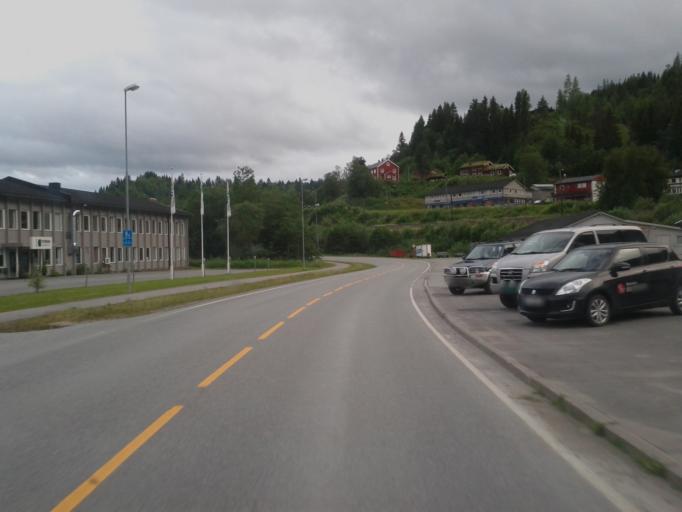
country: NO
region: Sor-Trondelag
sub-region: Midtre Gauldal
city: Storen
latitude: 63.0454
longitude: 10.2832
